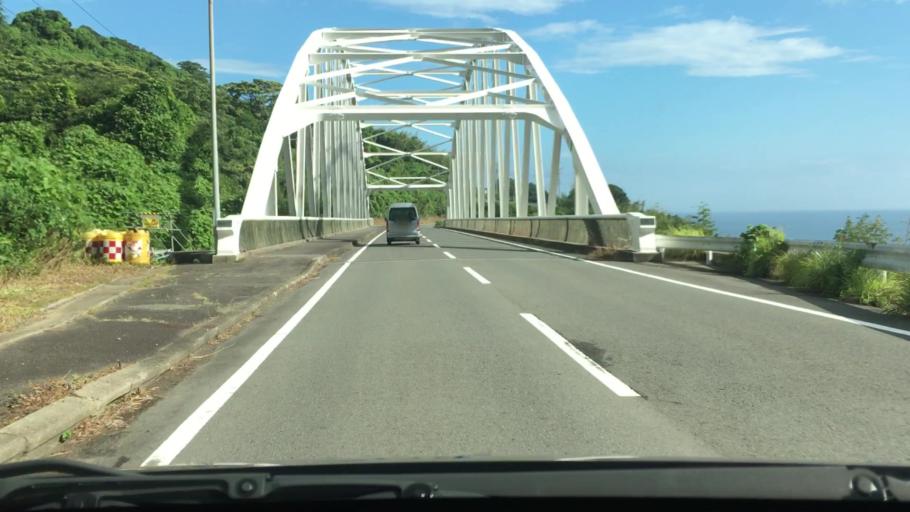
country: JP
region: Nagasaki
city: Togitsu
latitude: 32.8579
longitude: 129.6858
